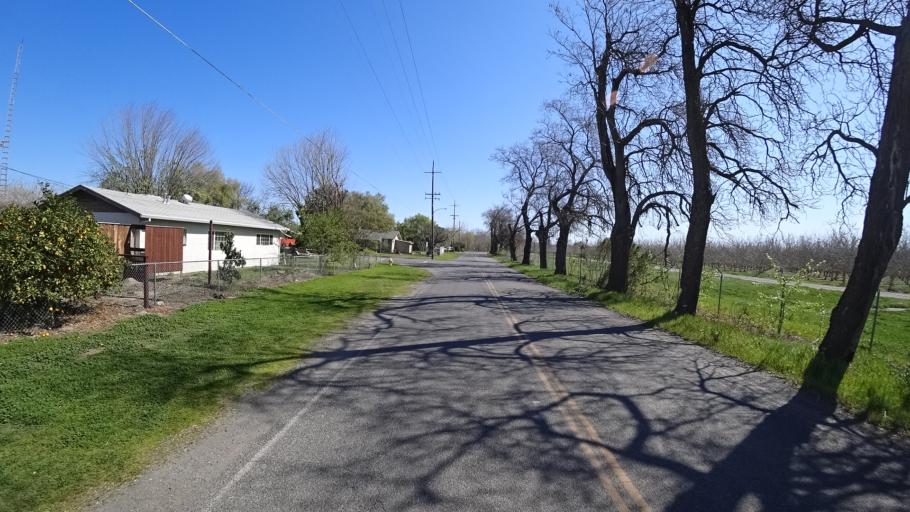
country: US
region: California
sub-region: Glenn County
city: Hamilton City
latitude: 39.7395
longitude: -122.0076
